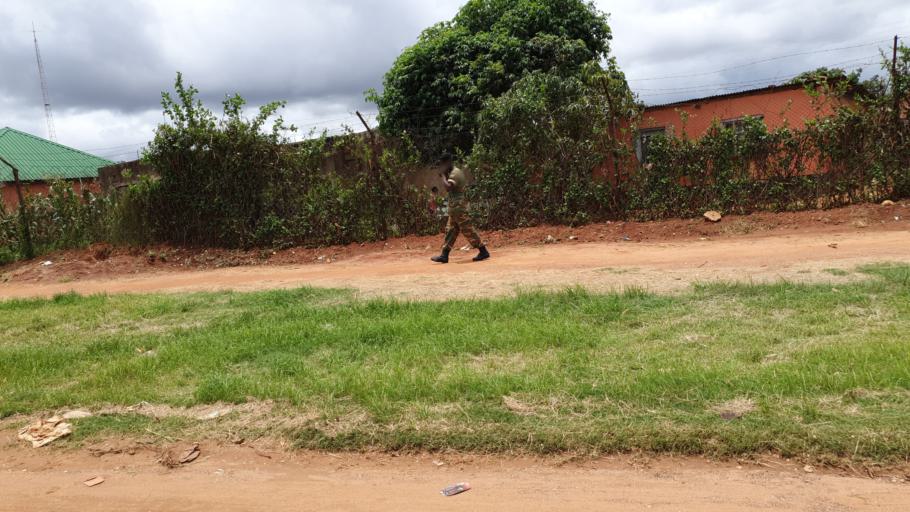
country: ZM
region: Lusaka
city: Lusaka
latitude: -15.4314
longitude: 28.3077
